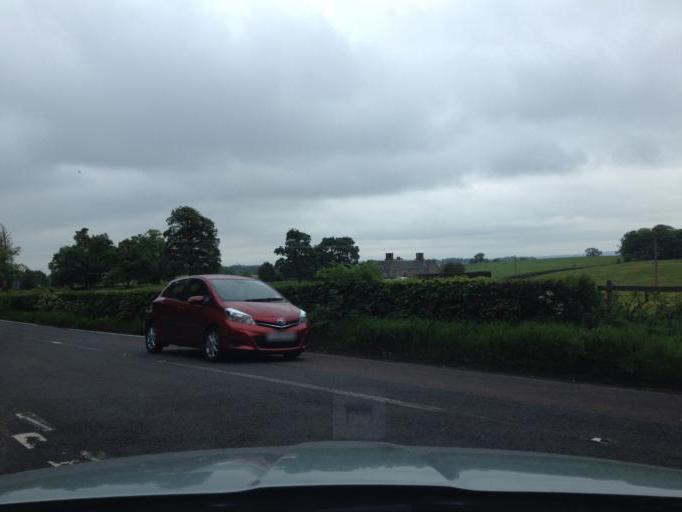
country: GB
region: Scotland
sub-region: Renfrewshire
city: Bishopton
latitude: 55.9163
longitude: -4.4895
